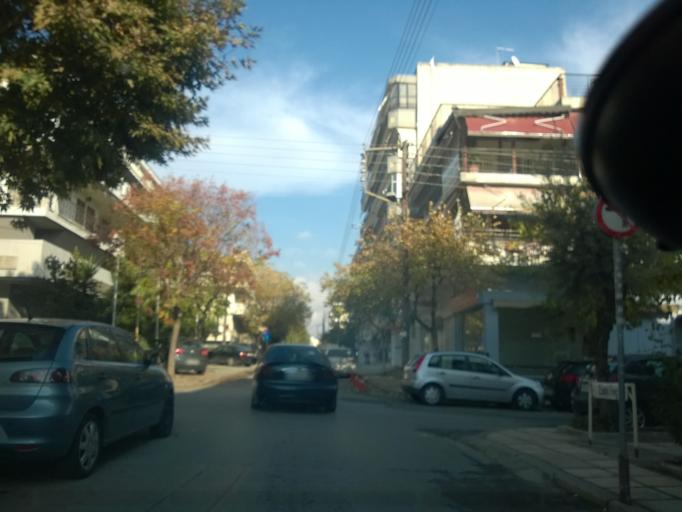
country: GR
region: Central Macedonia
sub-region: Nomos Thessalonikis
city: Stavroupoli
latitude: 40.6736
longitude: 22.9271
